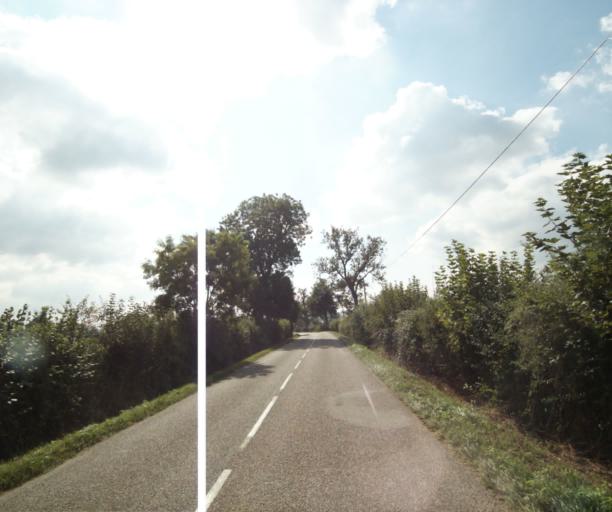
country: FR
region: Bourgogne
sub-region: Departement de Saone-et-Loire
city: Charolles
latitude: 46.3761
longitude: 4.2488
